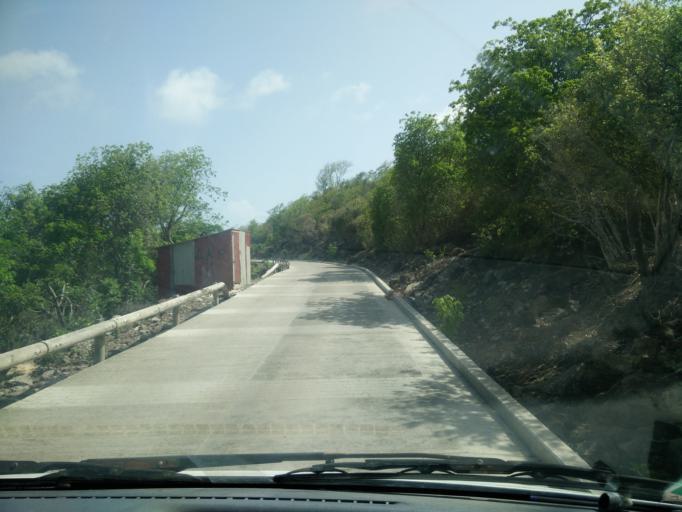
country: GP
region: Guadeloupe
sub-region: Guadeloupe
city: Terre-de-Bas
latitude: 15.8534
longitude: -61.6235
